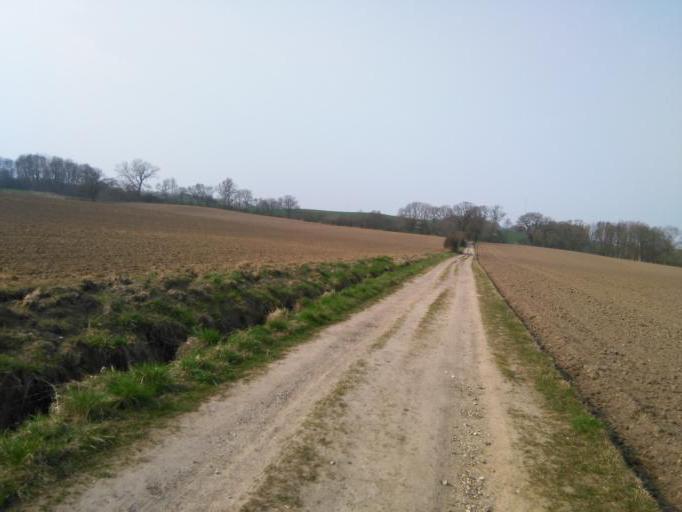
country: DK
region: Central Jutland
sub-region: Arhus Kommune
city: Beder
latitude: 56.0769
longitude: 10.2227
